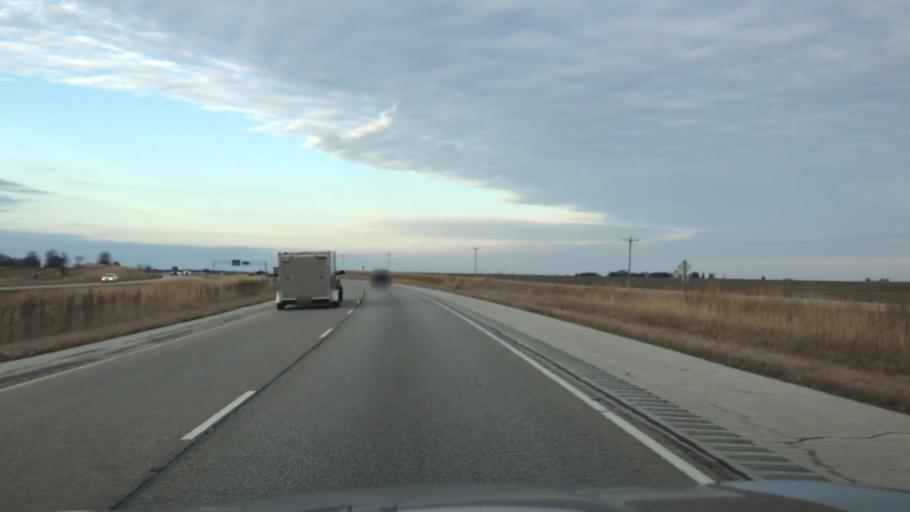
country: US
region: Illinois
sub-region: McLean County
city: Twin Grove
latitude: 40.3997
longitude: -89.0595
